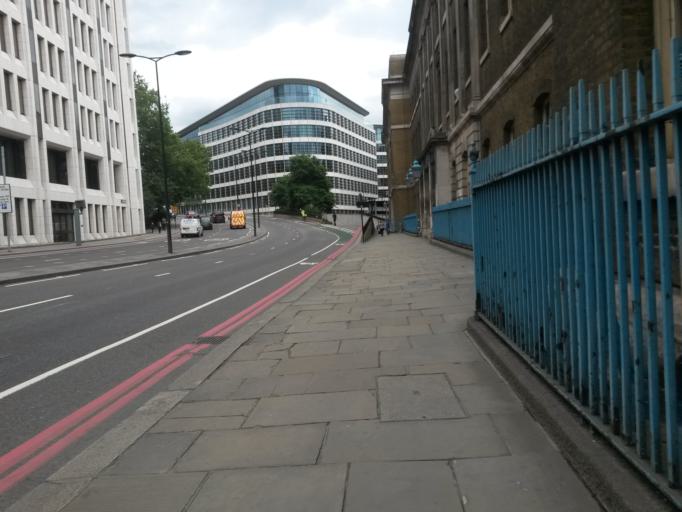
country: GB
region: England
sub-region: Greater London
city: City of London
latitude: 51.5091
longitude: -0.0827
